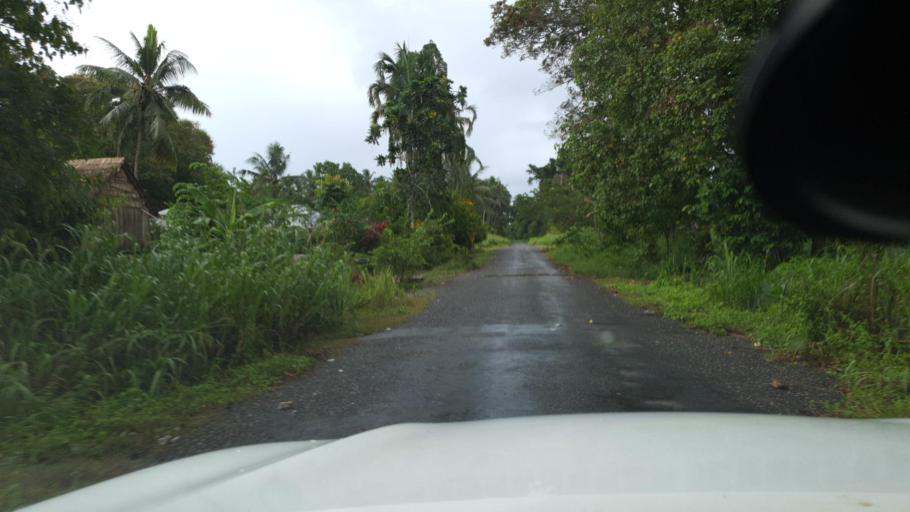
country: SB
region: Guadalcanal
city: Honiara
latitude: -9.4733
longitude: 160.3601
